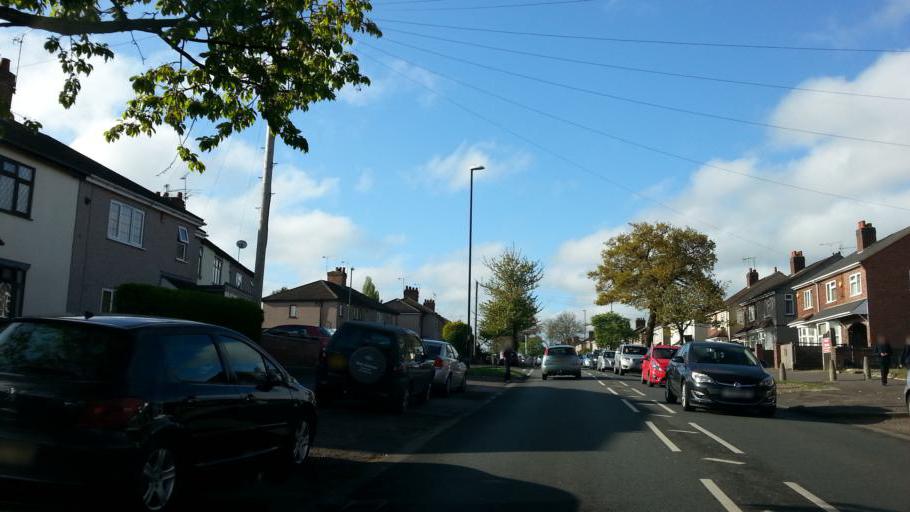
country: GB
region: England
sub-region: Warwickshire
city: Ryton on Dunsmore
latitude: 52.4103
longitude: -1.4443
